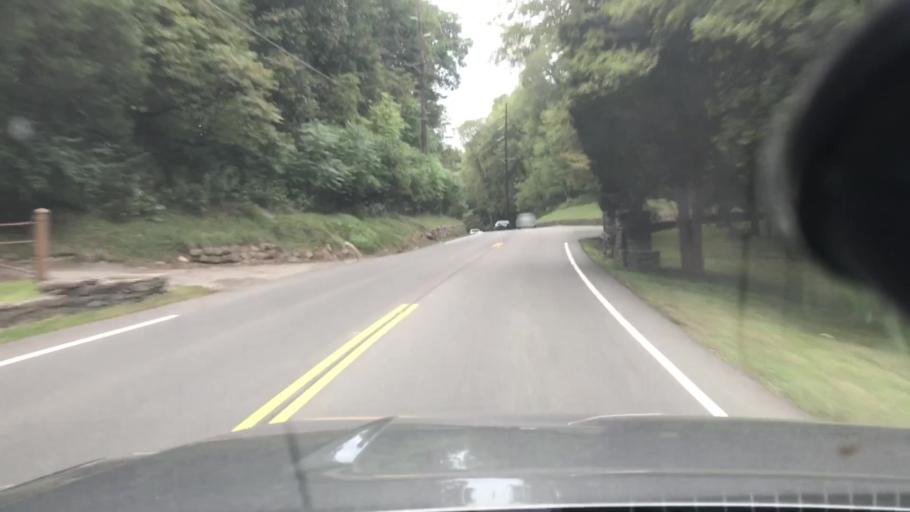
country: US
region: Tennessee
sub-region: Davidson County
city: Forest Hills
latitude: 36.0559
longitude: -86.9012
